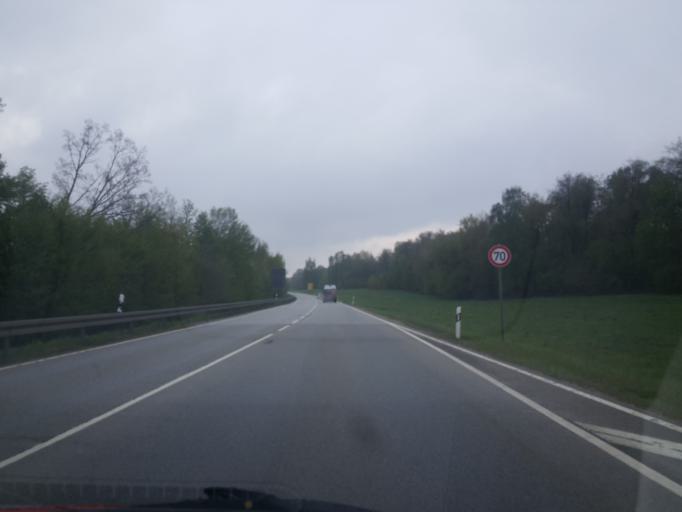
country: DE
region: Bavaria
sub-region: Lower Bavaria
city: Viechtach
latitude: 49.0740
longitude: 12.8809
